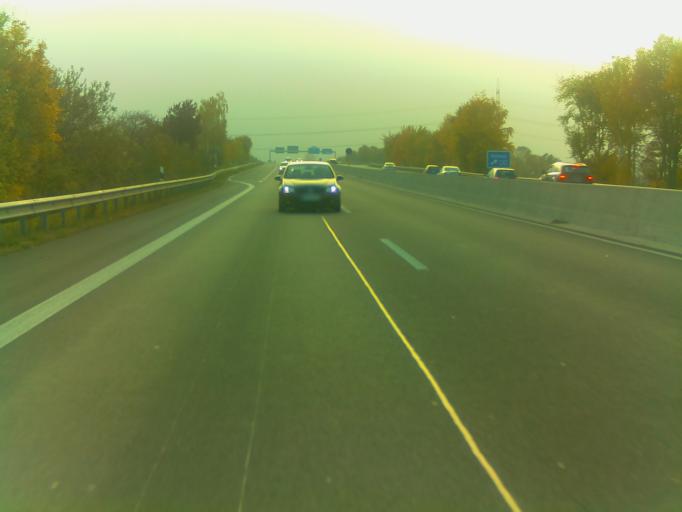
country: DE
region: Rheinland-Pfalz
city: Dannstadt-Schauernheim
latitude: 49.4453
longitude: 8.3309
